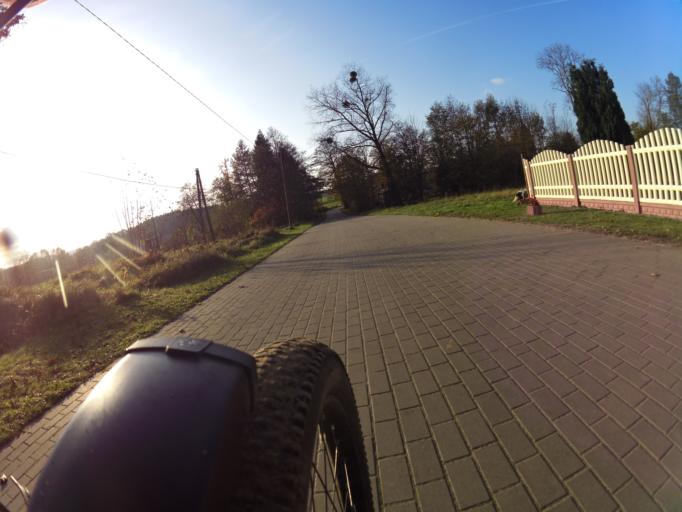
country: PL
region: Pomeranian Voivodeship
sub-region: Powiat pucki
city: Krokowa
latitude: 54.7502
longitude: 18.1921
